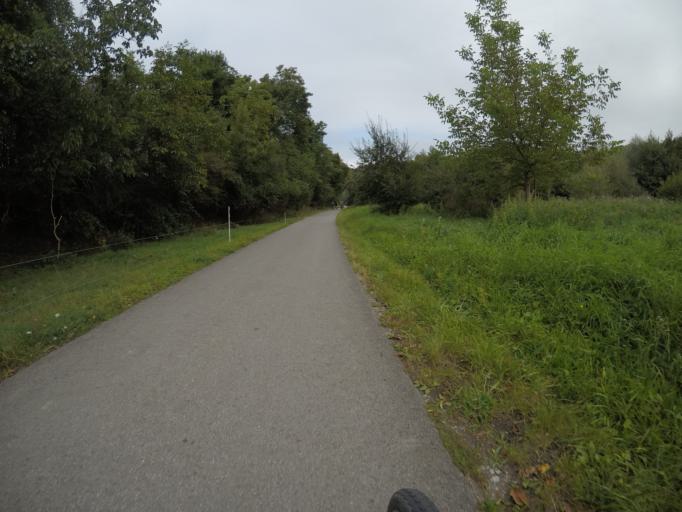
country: DE
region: Baden-Wuerttemberg
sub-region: Regierungsbezirk Stuttgart
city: Marbach am Neckar
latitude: 48.9080
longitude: 9.2561
